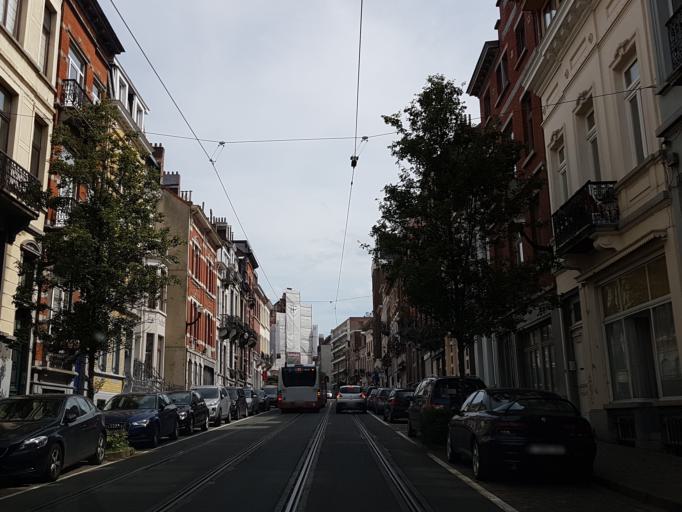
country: BE
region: Brussels Capital
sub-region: Bruxelles-Capitale
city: Brussels
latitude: 50.8215
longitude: 4.3760
